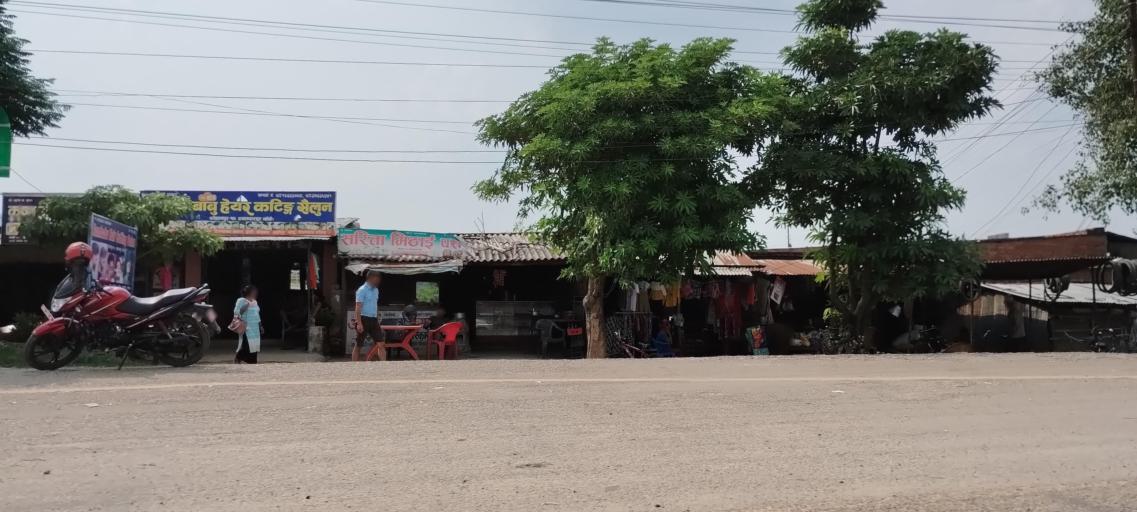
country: NP
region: Mid Western
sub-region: Bheri Zone
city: Nepalgunj
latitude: 28.1532
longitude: 81.6680
